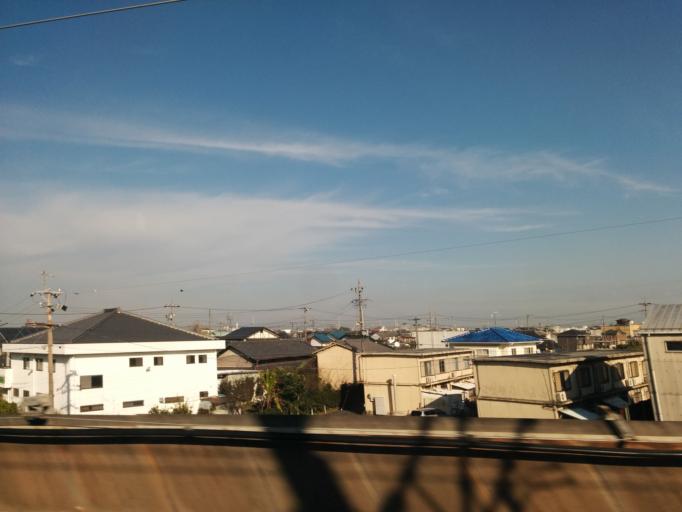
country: JP
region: Aichi
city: Sobue
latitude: 35.2771
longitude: 136.7499
